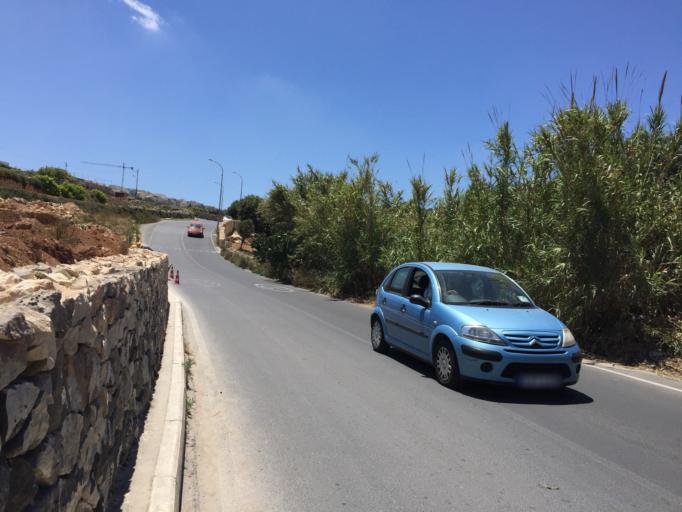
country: MT
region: Is-Swieqi
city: Swieqi
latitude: 35.9166
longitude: 14.4799
